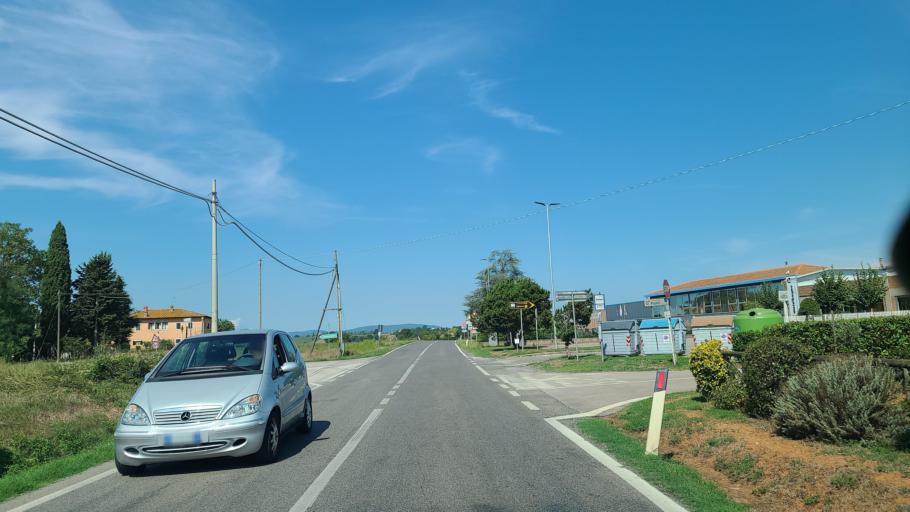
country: IT
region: Tuscany
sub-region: Provincia di Siena
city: Staggia
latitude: 43.3961
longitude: 11.1808
